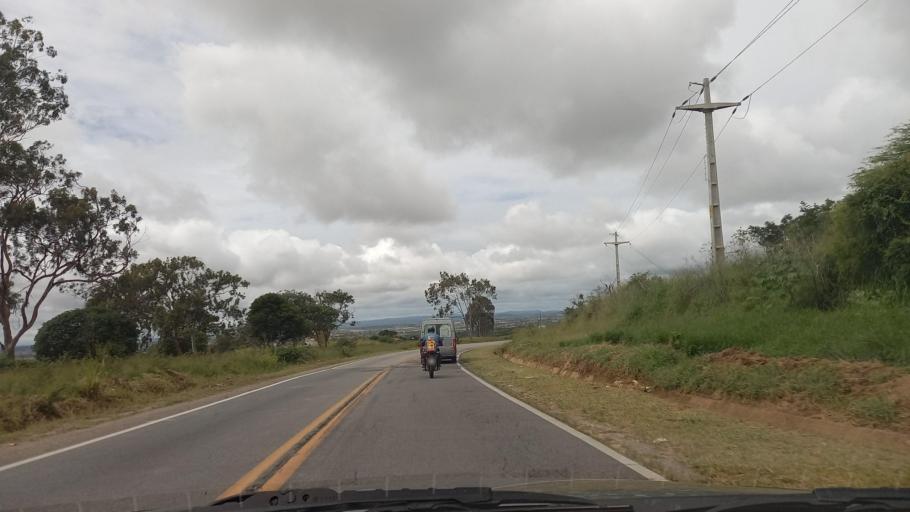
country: BR
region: Pernambuco
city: Garanhuns
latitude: -8.8770
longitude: -36.4489
